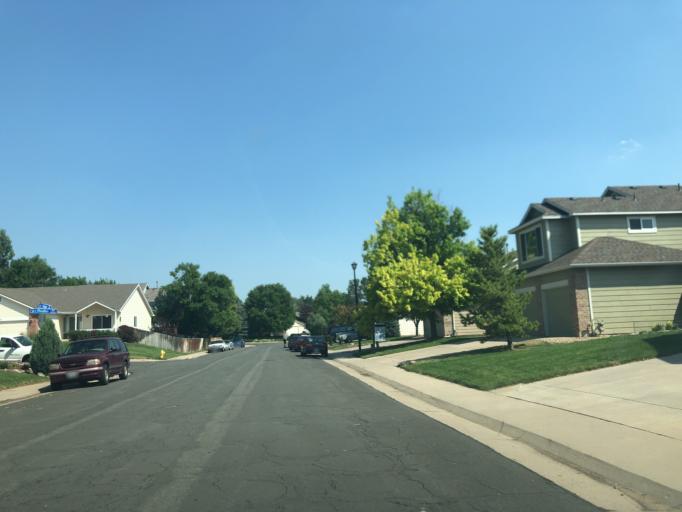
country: US
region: Colorado
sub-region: Arapahoe County
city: Dove Valley
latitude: 39.6321
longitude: -104.7594
